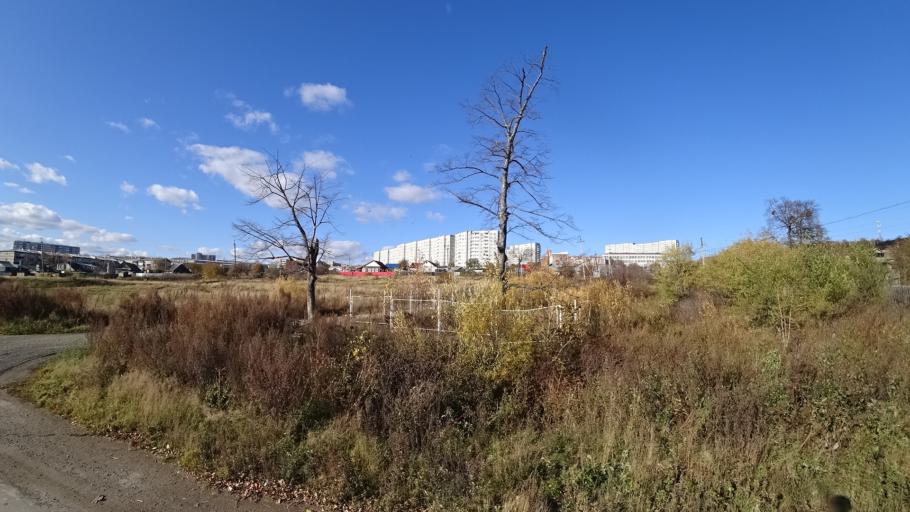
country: RU
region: Khabarovsk Krai
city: Amursk
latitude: 50.2354
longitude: 136.9153
